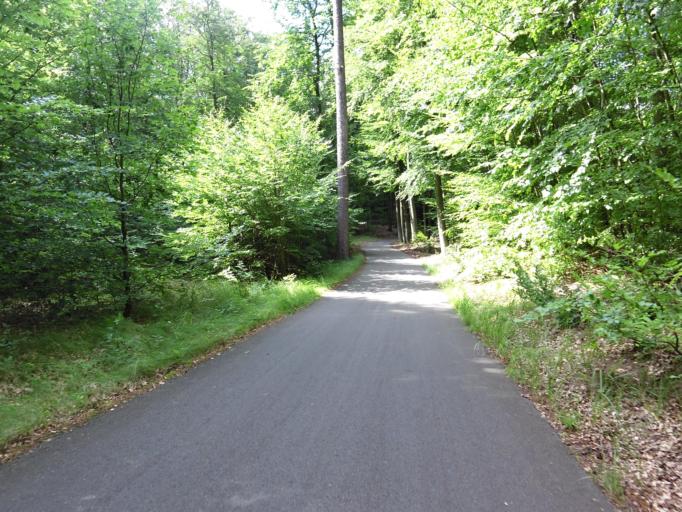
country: DE
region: Brandenburg
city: Lychen
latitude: 53.1863
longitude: 13.3463
